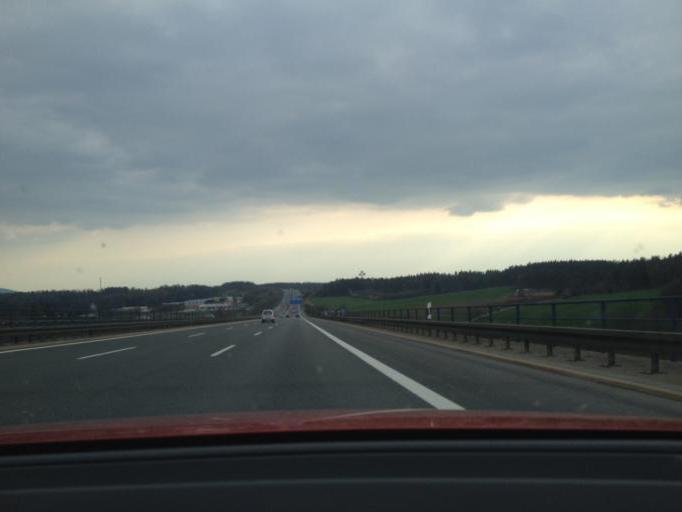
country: DE
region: Bavaria
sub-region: Regierungsbezirk Mittelfranken
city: Schnaittach
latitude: 49.5774
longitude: 11.3420
